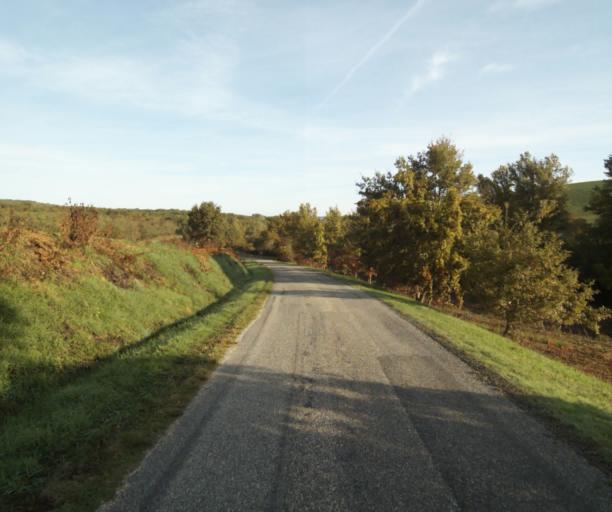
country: FR
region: Midi-Pyrenees
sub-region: Departement du Tarn-et-Garonne
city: Nohic
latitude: 43.9237
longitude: 1.4823
